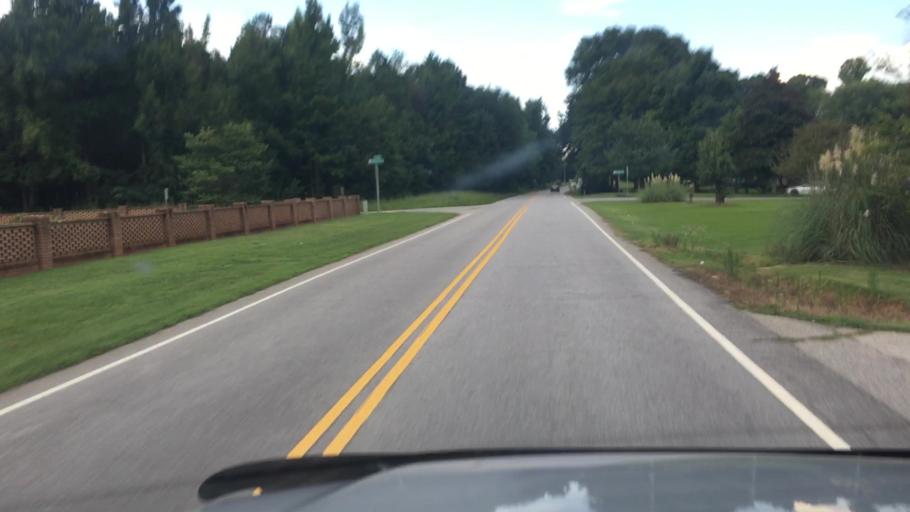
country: US
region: South Carolina
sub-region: Spartanburg County
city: Mayo
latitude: 35.1172
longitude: -81.8546
